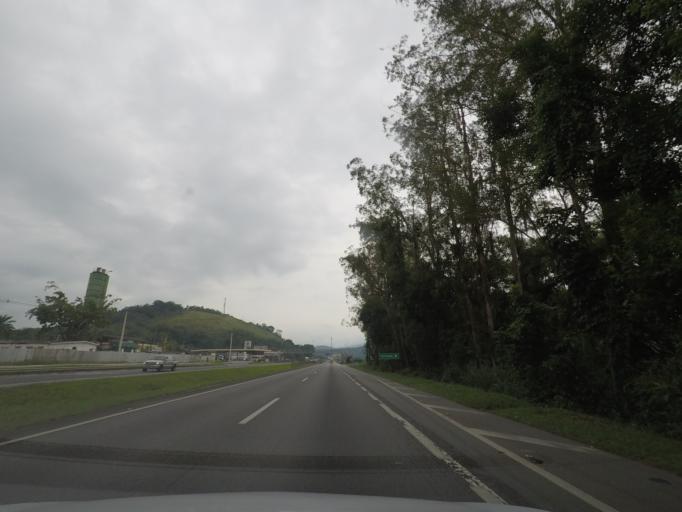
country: BR
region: Sao Paulo
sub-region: Miracatu
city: Miracatu
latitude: -24.1506
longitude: -47.3143
